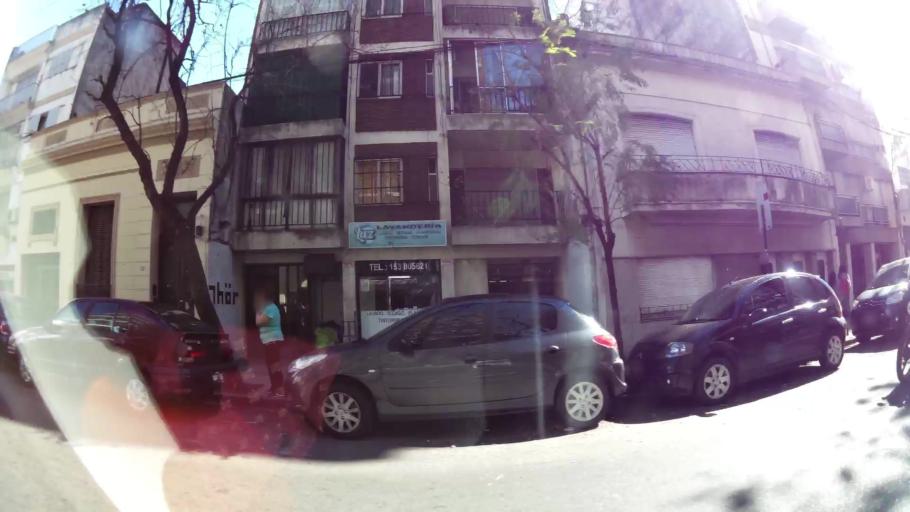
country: AR
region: Santa Fe
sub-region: Departamento de Rosario
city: Rosario
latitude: -32.9493
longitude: -60.6438
